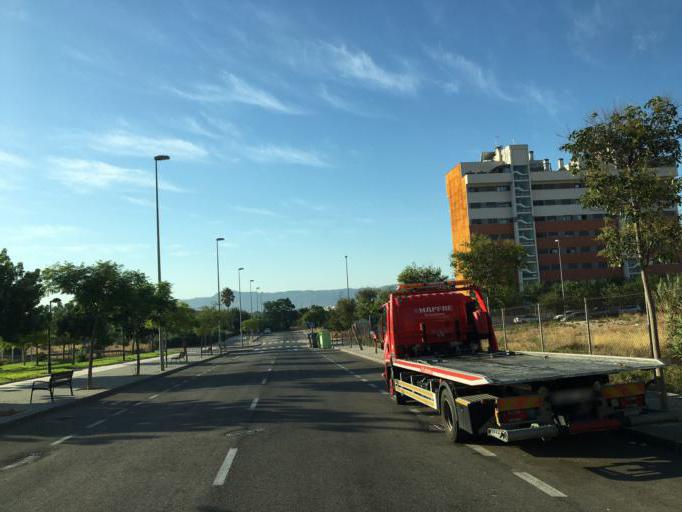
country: ES
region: Murcia
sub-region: Murcia
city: Murcia
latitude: 38.0157
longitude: -1.1483
